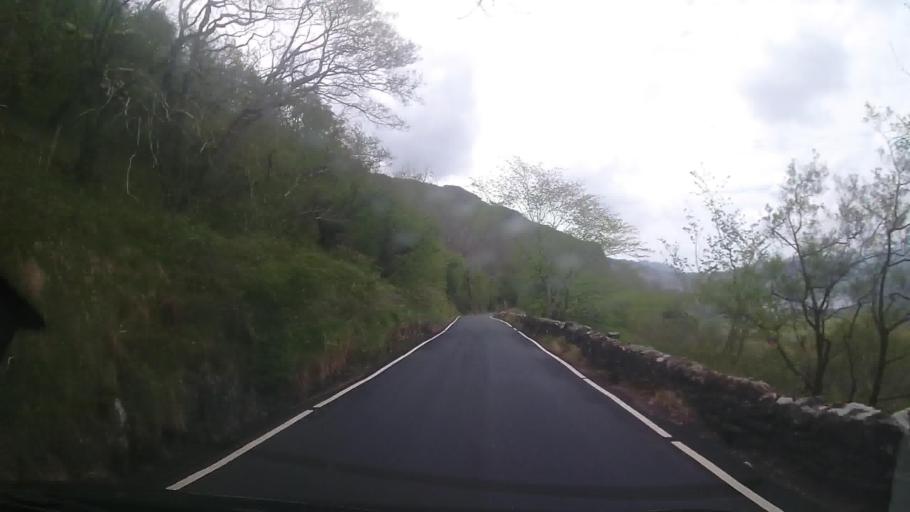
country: GB
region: Wales
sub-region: Gwynedd
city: Blaenau-Ffestiniog
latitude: 53.0631
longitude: -4.0017
